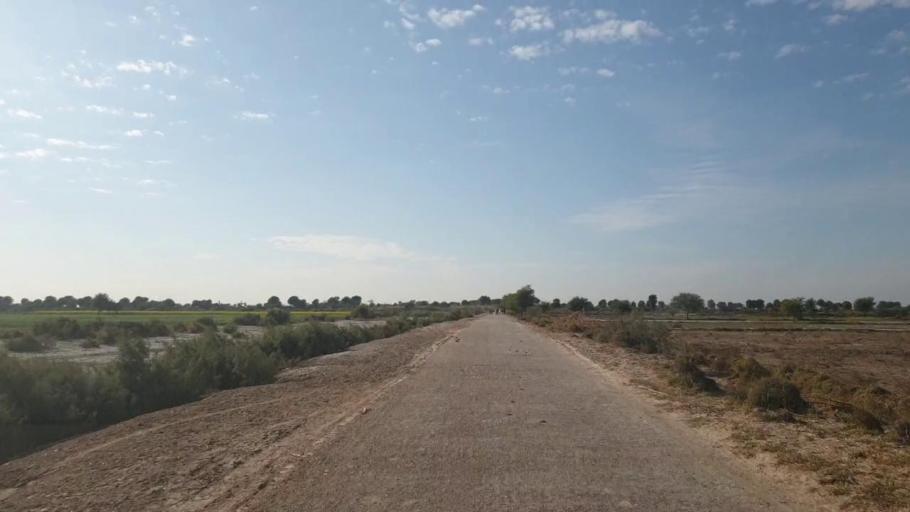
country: PK
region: Sindh
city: Sanghar
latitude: 26.0737
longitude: 68.8768
